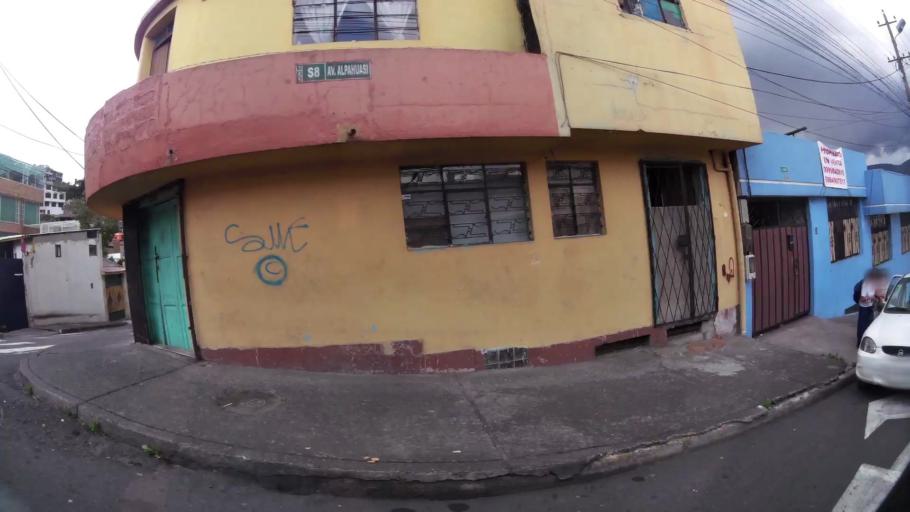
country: EC
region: Pichincha
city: Quito
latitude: -0.2475
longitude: -78.5085
